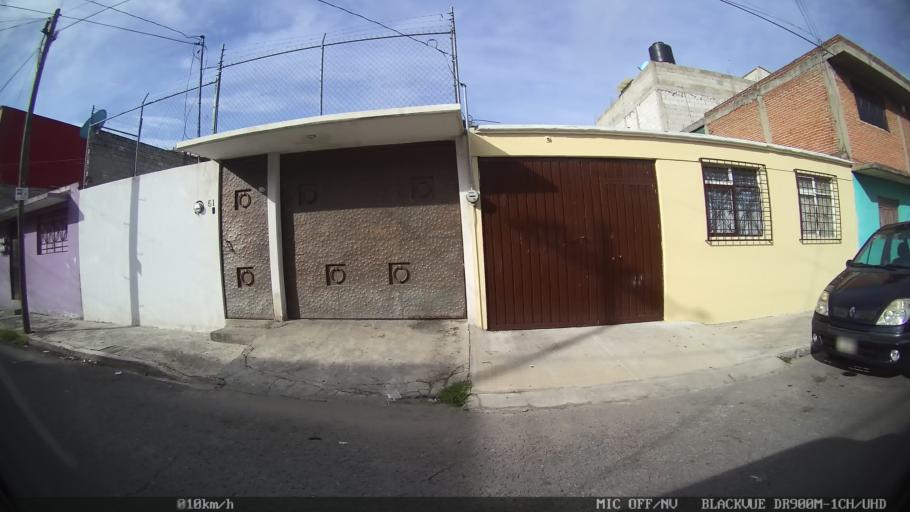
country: MX
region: Puebla
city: Puebla
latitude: 19.0731
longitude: -98.1812
